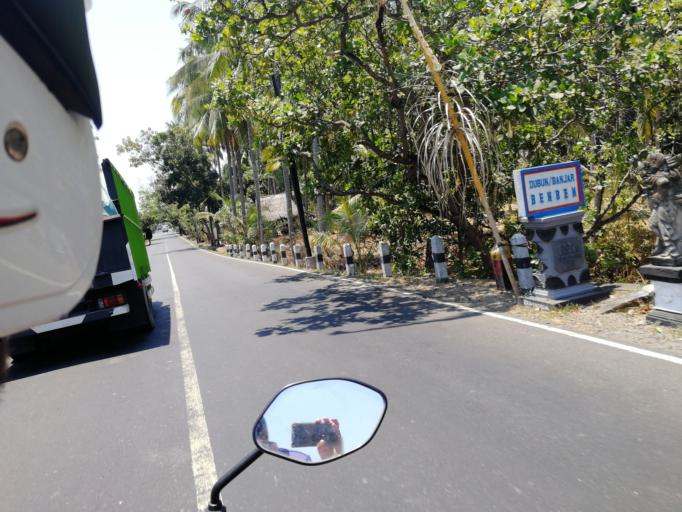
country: ID
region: Bali
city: Banjar Trunyan
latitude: -8.1490
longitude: 115.4075
